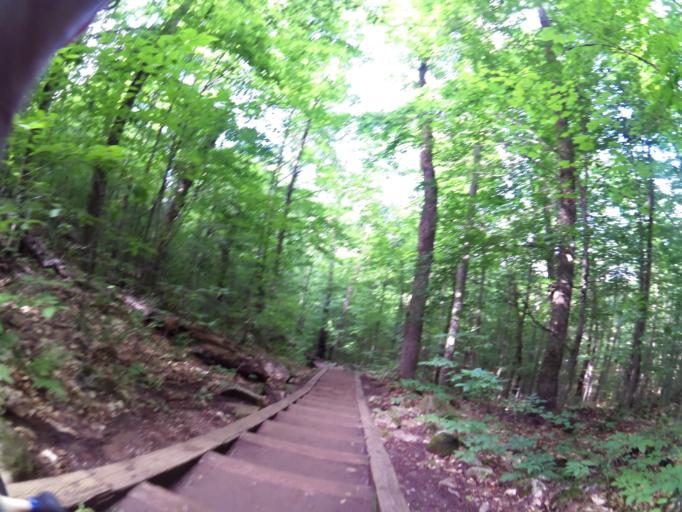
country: CA
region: Quebec
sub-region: Outaouais
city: Wakefield
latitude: 45.5855
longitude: -75.9796
